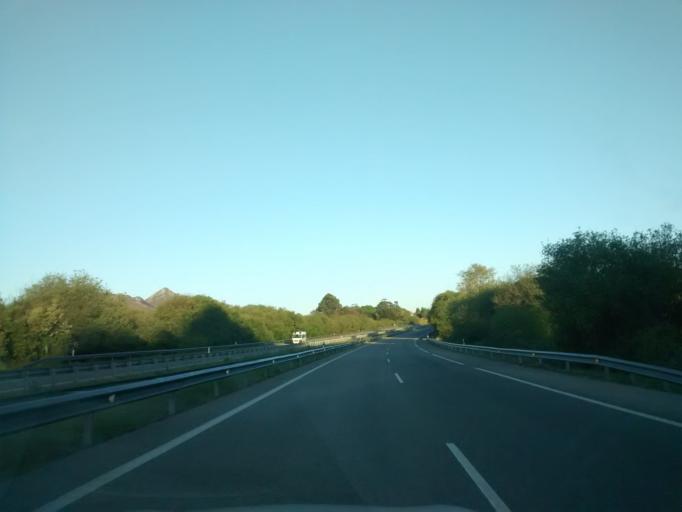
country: ES
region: Asturias
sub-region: Province of Asturias
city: Carrena
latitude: 43.4436
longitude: -4.9082
